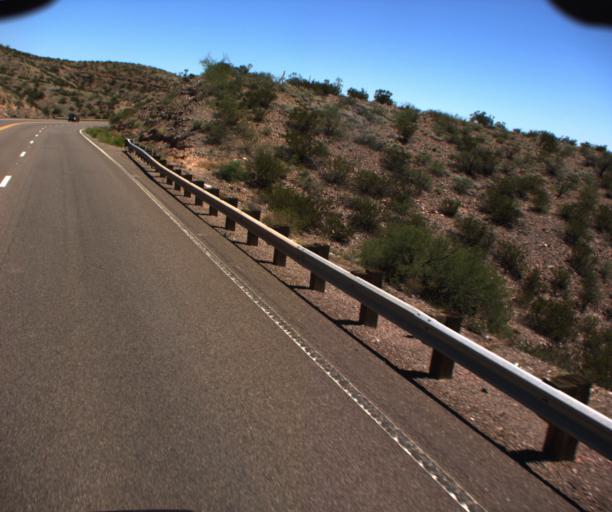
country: US
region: Arizona
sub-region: Greenlee County
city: Clifton
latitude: 33.0146
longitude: -109.2855
